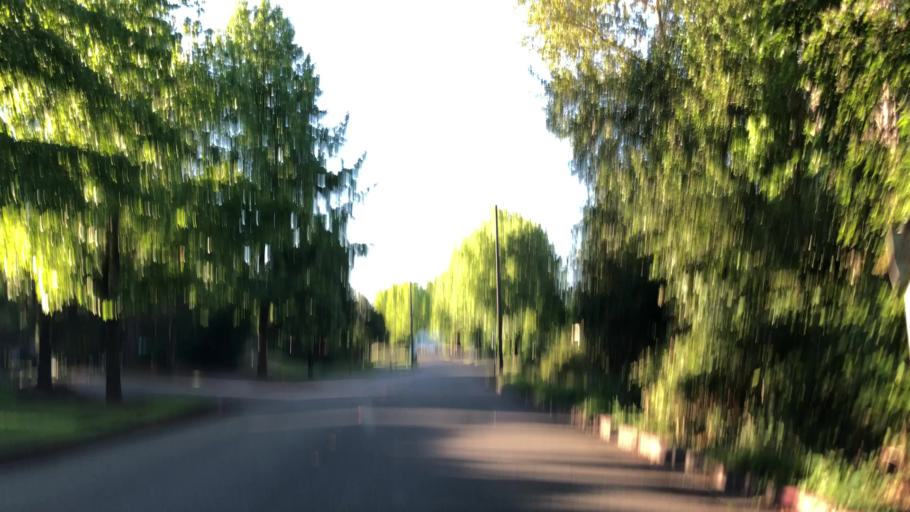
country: US
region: Washington
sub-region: King County
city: Bothell
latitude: 47.7954
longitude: -122.2108
